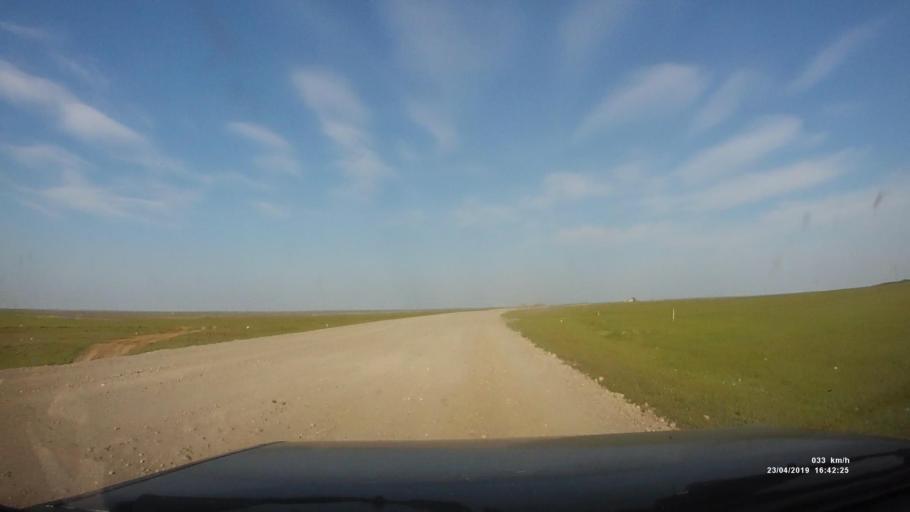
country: RU
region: Kalmykiya
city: Priyutnoye
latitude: 46.3478
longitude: 43.1937
